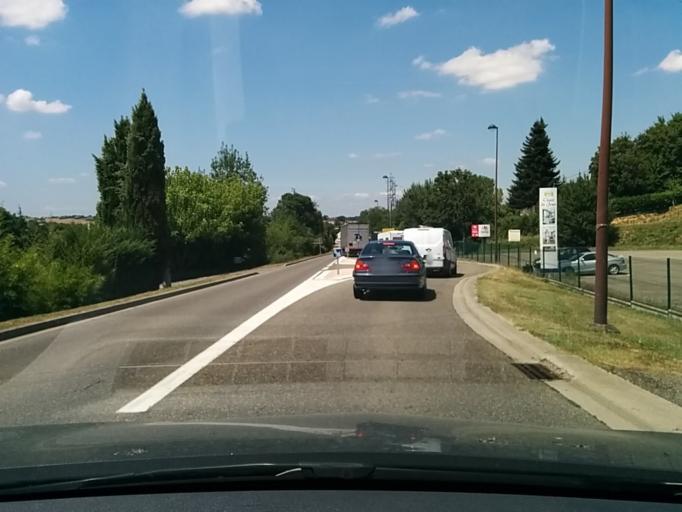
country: FR
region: Midi-Pyrenees
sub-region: Departement du Gers
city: Vic-Fezensac
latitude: 43.7520
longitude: 0.3136
